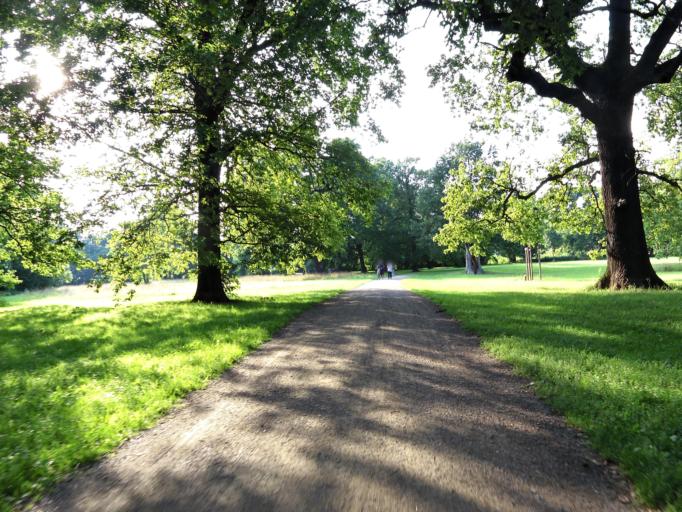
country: DE
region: Saxony
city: Leipzig
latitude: 51.3138
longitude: 12.3311
